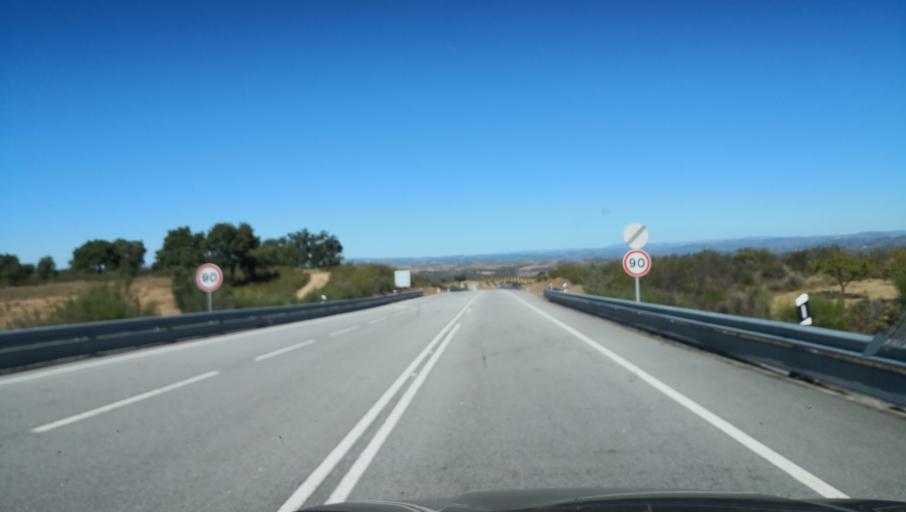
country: PT
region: Braganca
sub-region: Mirandela
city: Mirandela
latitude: 41.4820
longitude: -7.2245
